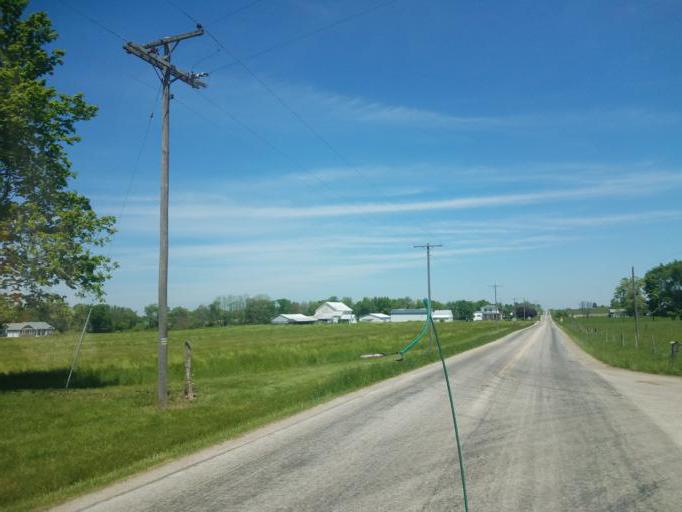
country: US
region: Ohio
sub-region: Ashland County
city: Ashland
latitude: 40.9302
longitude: -82.2433
